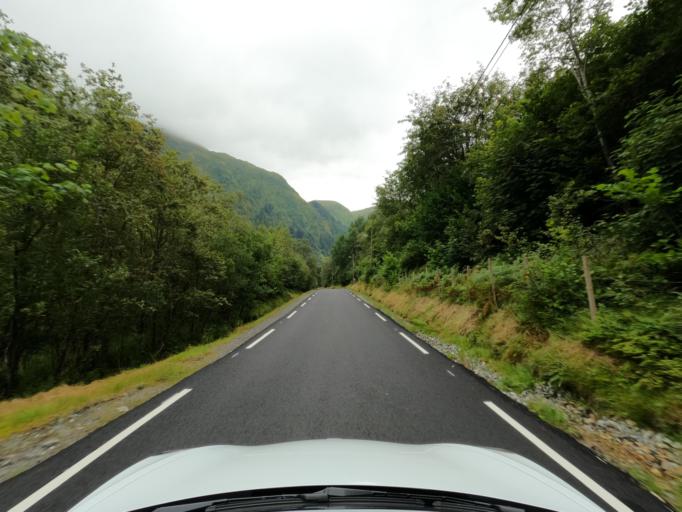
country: NO
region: Hordaland
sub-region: Bergen
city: Espeland
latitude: 60.3710
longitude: 5.4932
